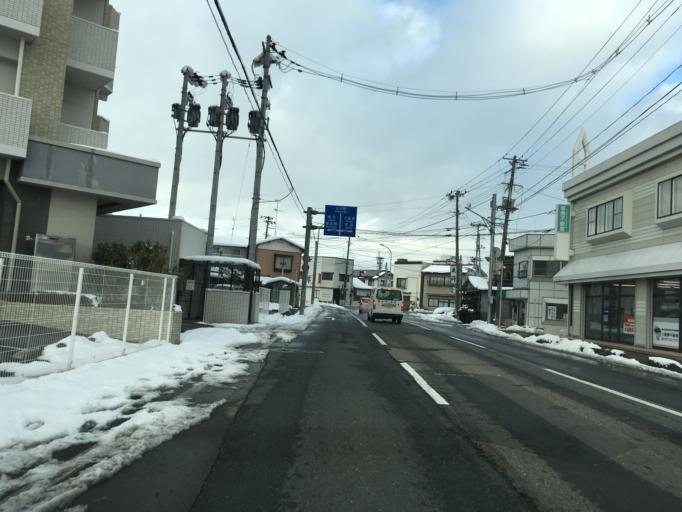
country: JP
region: Iwate
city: Mizusawa
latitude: 39.1361
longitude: 141.1450
